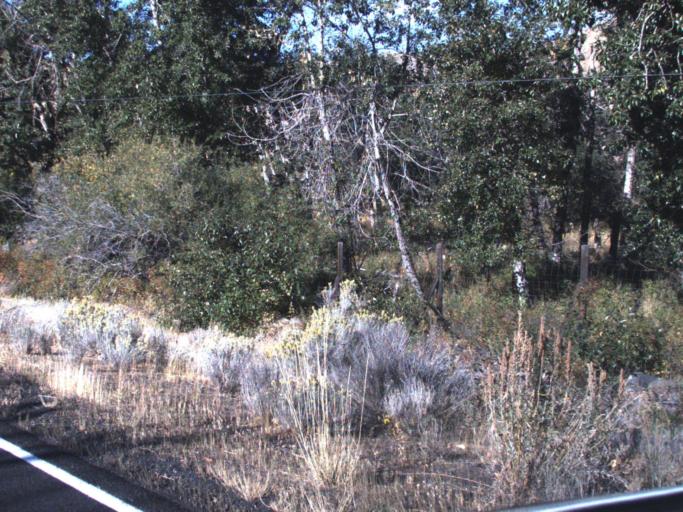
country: US
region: Washington
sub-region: Yakima County
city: Tieton
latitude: 46.7300
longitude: -120.8041
